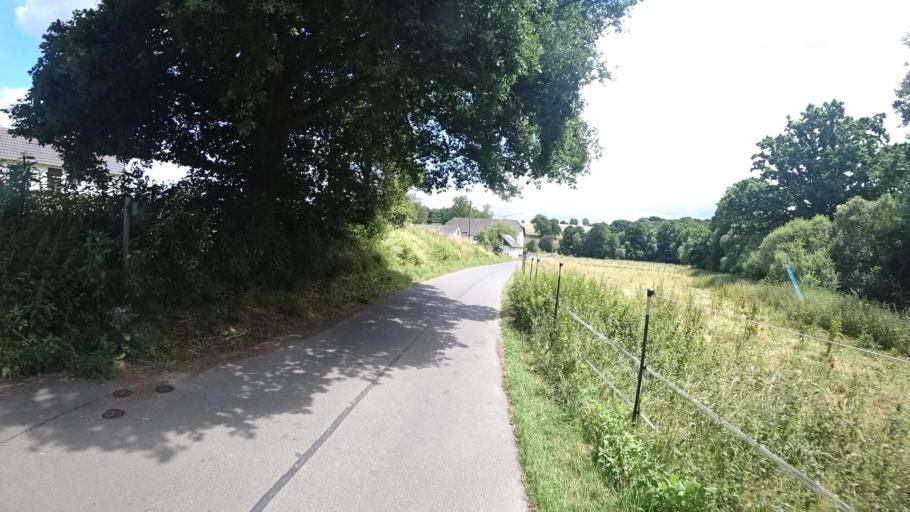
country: DE
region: Rheinland-Pfalz
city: Ersfeld
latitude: 50.6957
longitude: 7.5204
